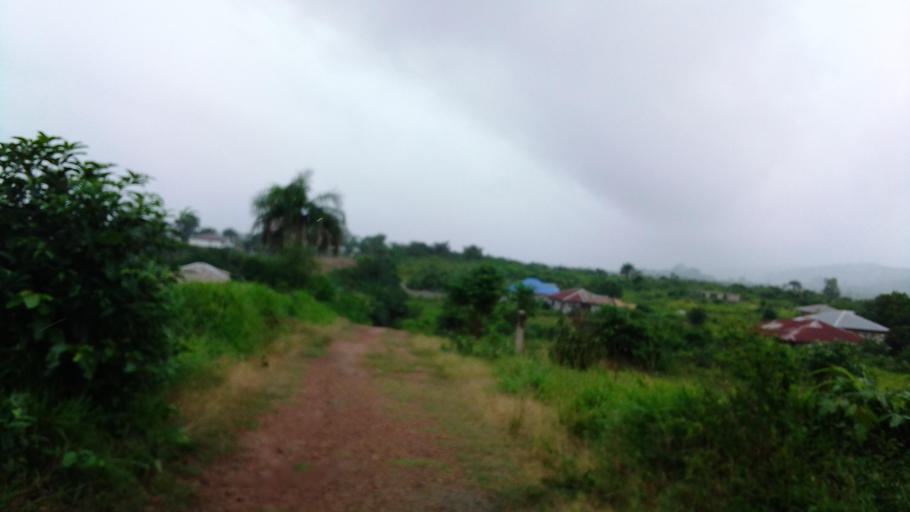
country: SL
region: Eastern Province
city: Kenema
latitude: 7.8334
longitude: -11.2112
